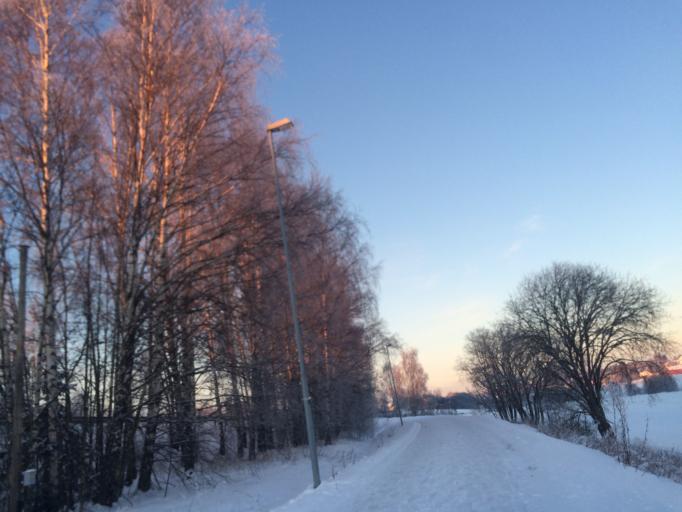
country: NO
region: Akershus
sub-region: Ski
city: Ski
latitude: 59.6971
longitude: 10.8327
